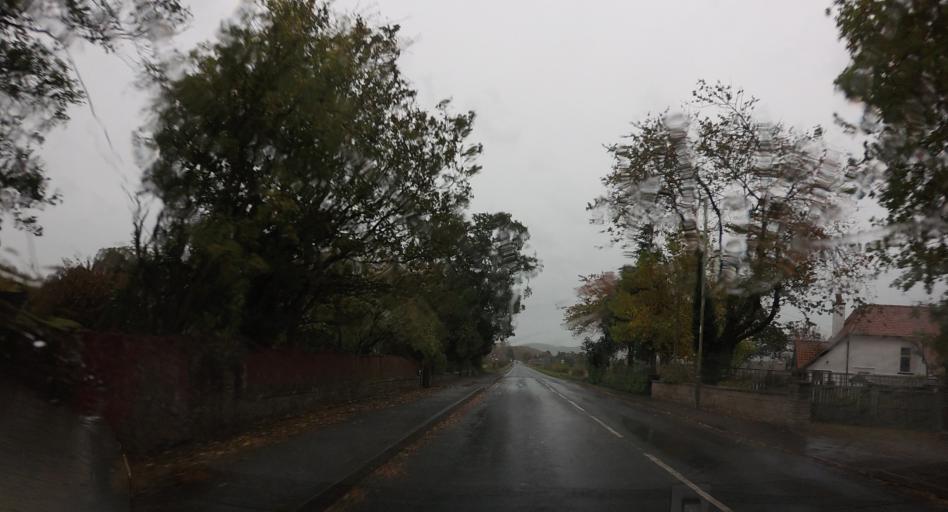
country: GB
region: Scotland
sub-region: Perth and Kinross
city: Coupar Angus
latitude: 56.5425
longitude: -3.2641
